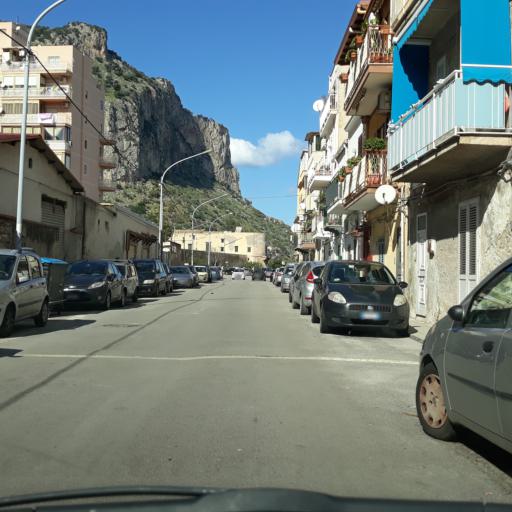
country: IT
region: Sicily
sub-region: Palermo
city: Palermo
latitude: 38.1642
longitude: 13.3696
